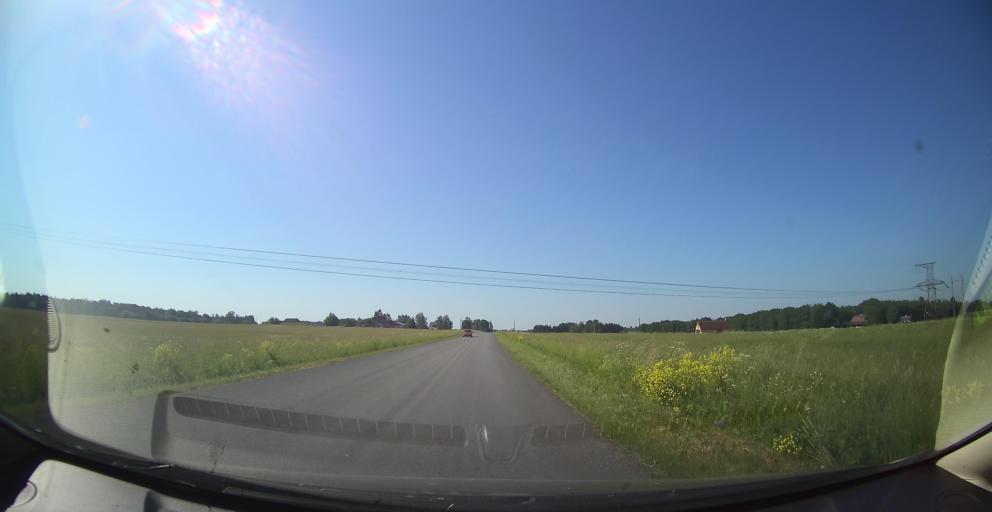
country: EE
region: Harju
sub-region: Raasiku vald
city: Raasiku
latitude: 59.2742
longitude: 25.1347
